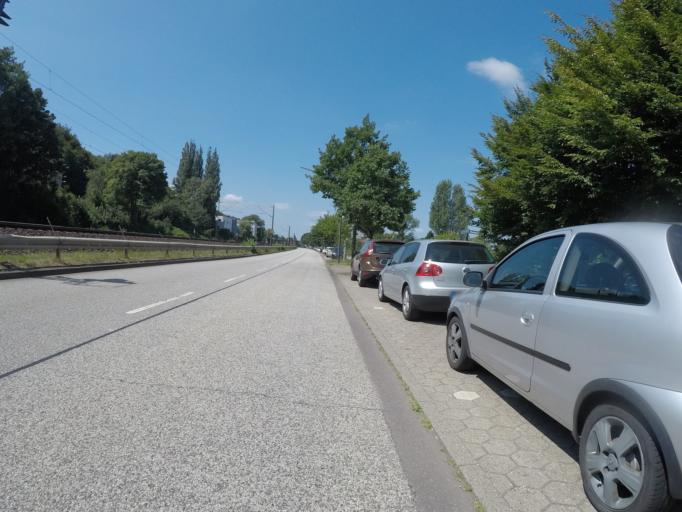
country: DE
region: Hamburg
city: Harburg
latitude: 53.4718
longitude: 9.9454
